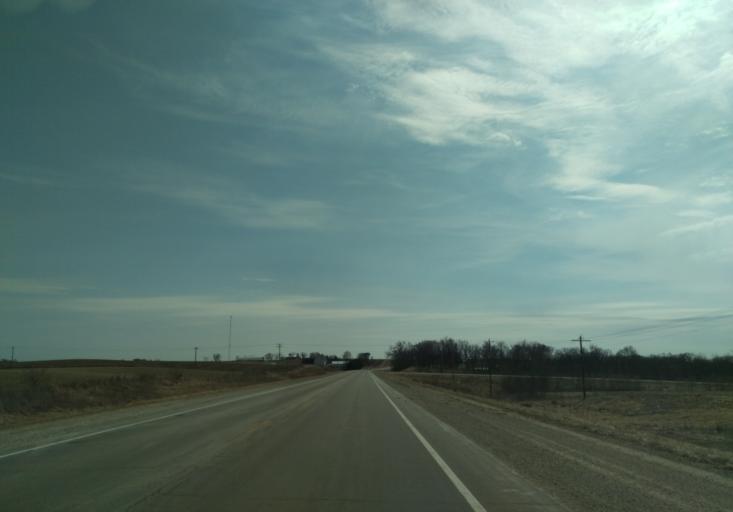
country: US
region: Iowa
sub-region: Winneshiek County
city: Decorah
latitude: 43.4309
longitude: -91.8599
